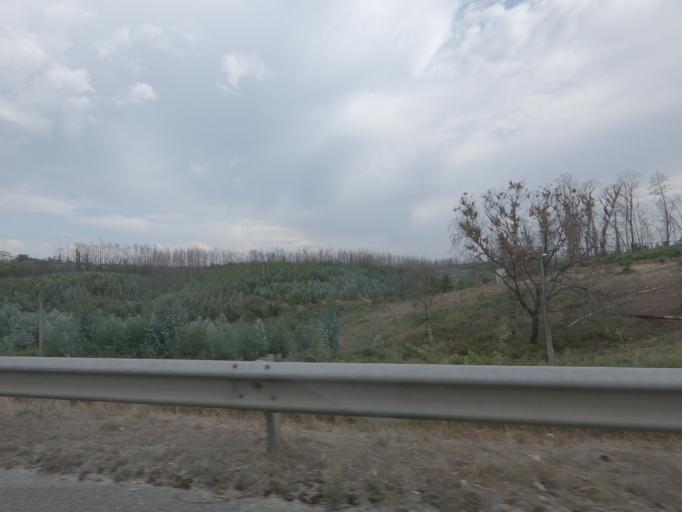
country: PT
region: Viseu
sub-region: Santa Comba Dao
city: Santa Comba Dao
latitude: 40.3561
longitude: -8.1450
